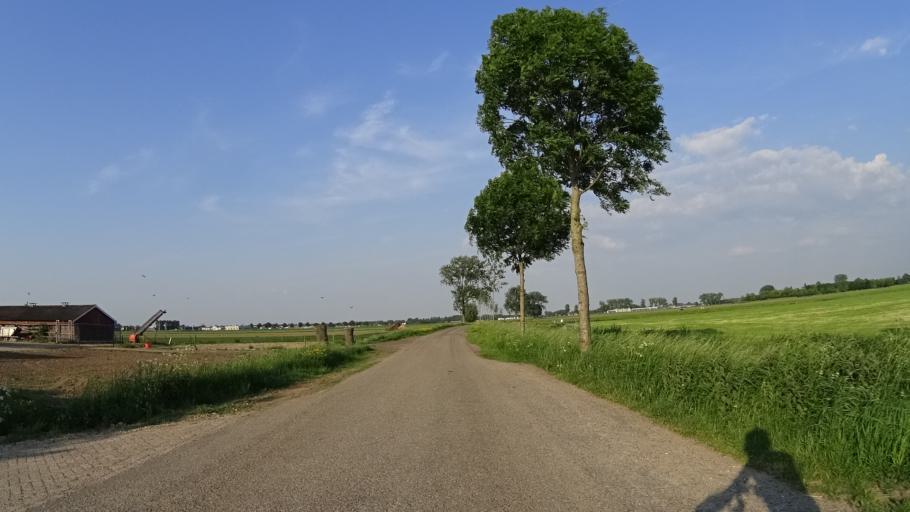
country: NL
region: North Brabant
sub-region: Gemeente Aalburg
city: Aalburg
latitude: 51.7643
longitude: 5.0818
